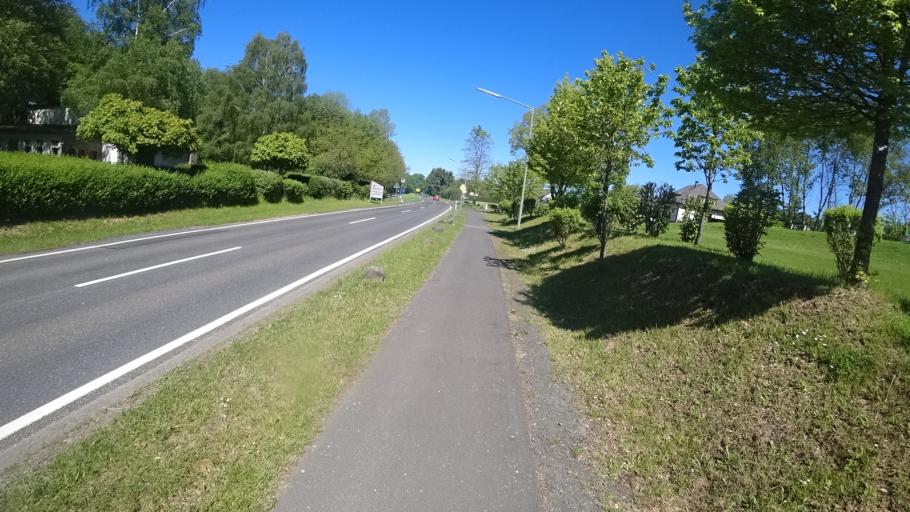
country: DE
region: Rheinland-Pfalz
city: Elkenroth
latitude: 50.7321
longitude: 7.8824
